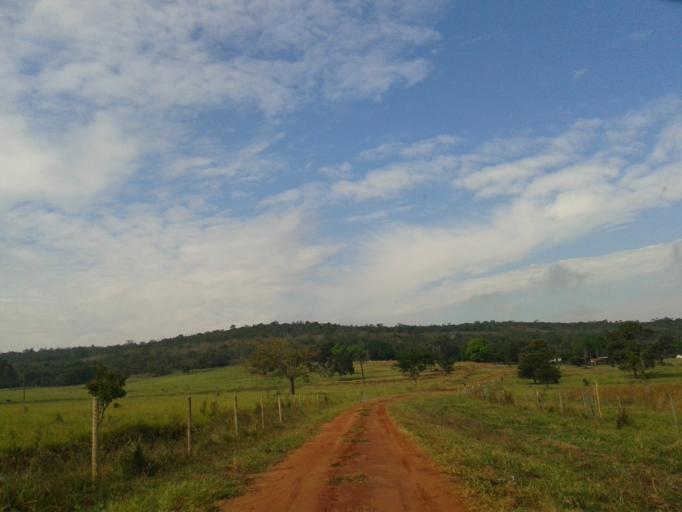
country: BR
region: Minas Gerais
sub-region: Campina Verde
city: Campina Verde
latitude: -19.3934
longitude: -49.6263
